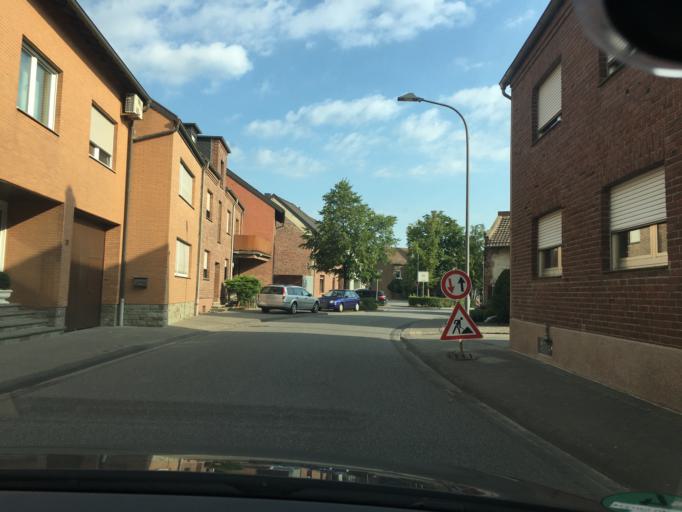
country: DE
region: North Rhine-Westphalia
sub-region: Regierungsbezirk Koln
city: Inden
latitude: 50.8760
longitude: 6.3965
